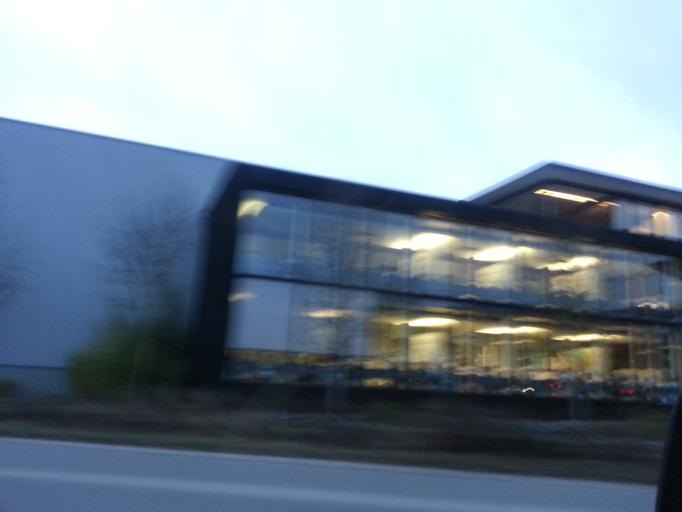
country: DE
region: Baden-Wuerttemberg
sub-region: Tuebingen Region
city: Markdorf
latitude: 47.7164
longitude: 9.3962
